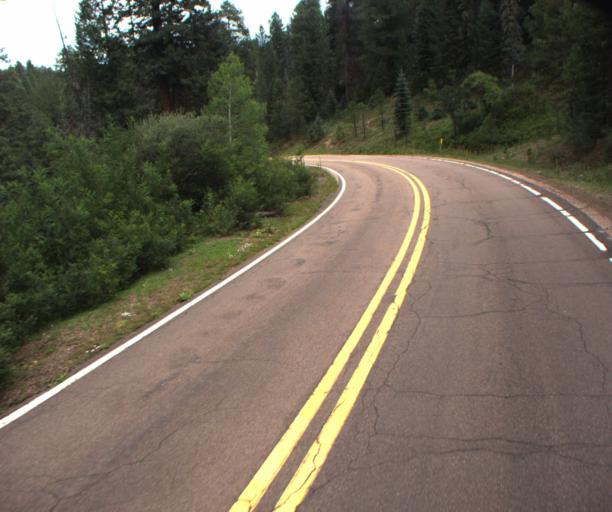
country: US
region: Arizona
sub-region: Navajo County
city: Pinetop-Lakeside
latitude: 34.0443
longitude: -109.7307
